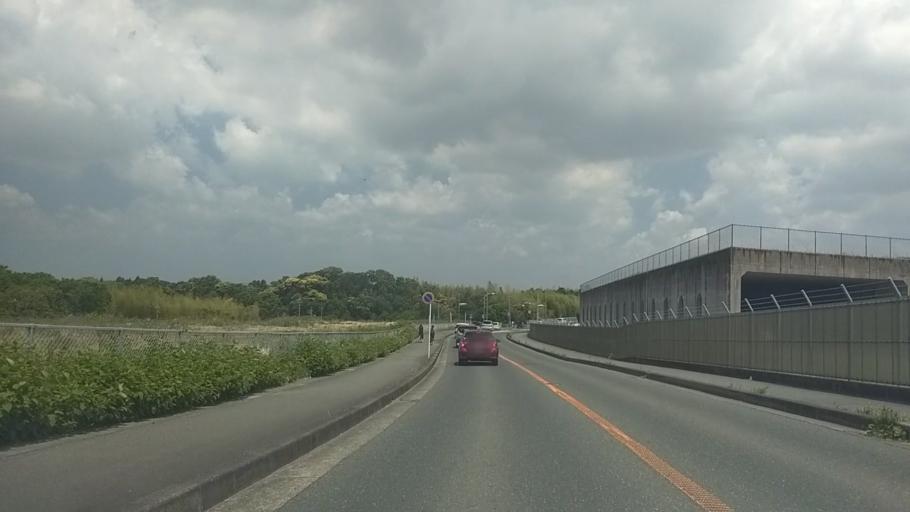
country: JP
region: Shizuoka
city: Hamamatsu
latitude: 34.7500
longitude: 137.6855
